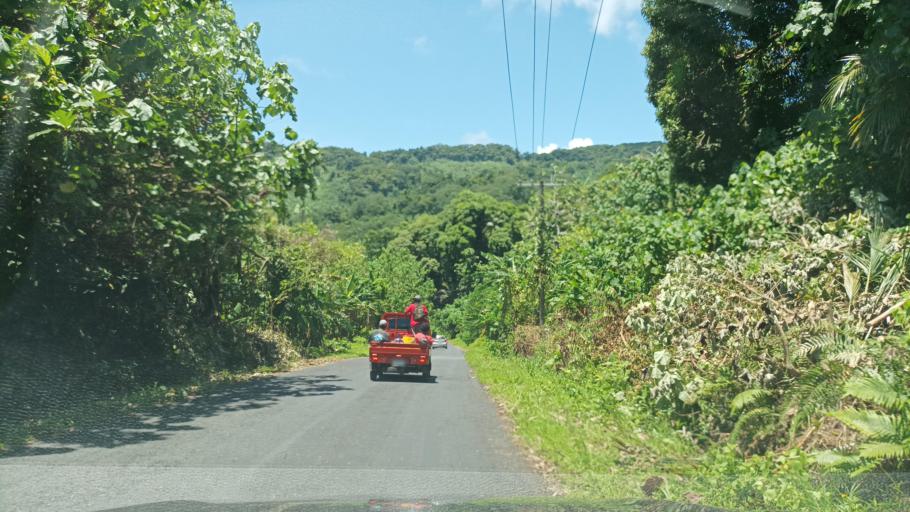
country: FM
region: Pohnpei
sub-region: Madolenihm Municipality
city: Madolenihm Municipality Government
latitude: 6.9201
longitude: 158.3113
